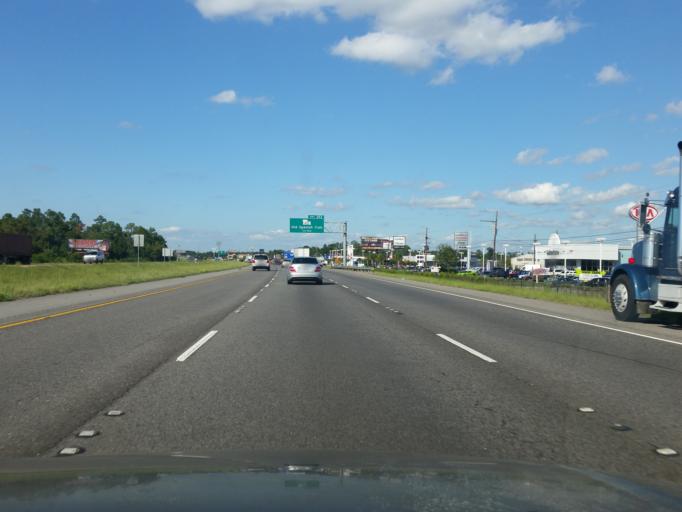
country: US
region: Louisiana
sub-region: Saint Tammany Parish
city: Eden Isle
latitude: 30.2367
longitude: -89.7684
